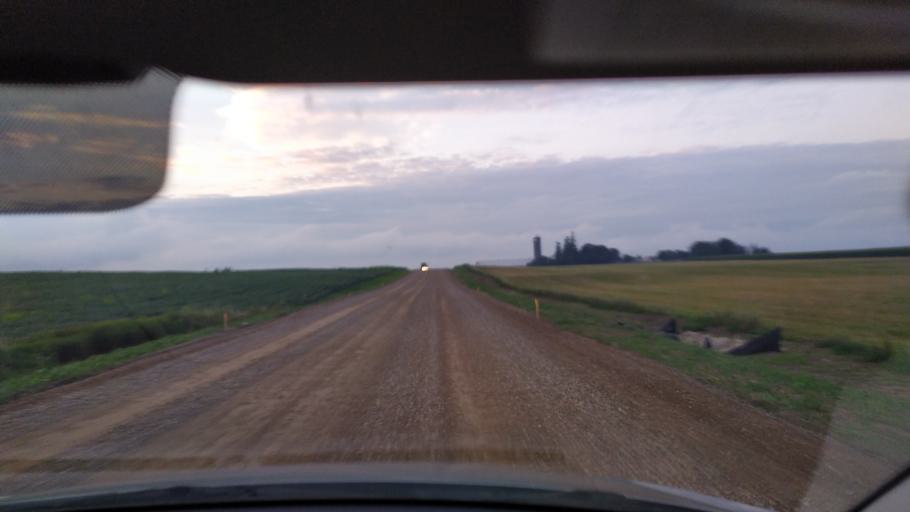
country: CA
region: Ontario
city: Kitchener
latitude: 43.3251
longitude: -80.6174
